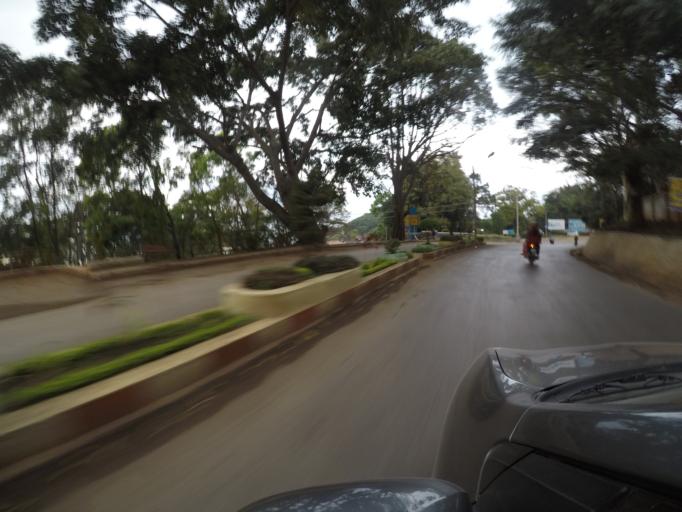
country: MM
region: Shan
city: Taunggyi
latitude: 20.8177
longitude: 97.0342
